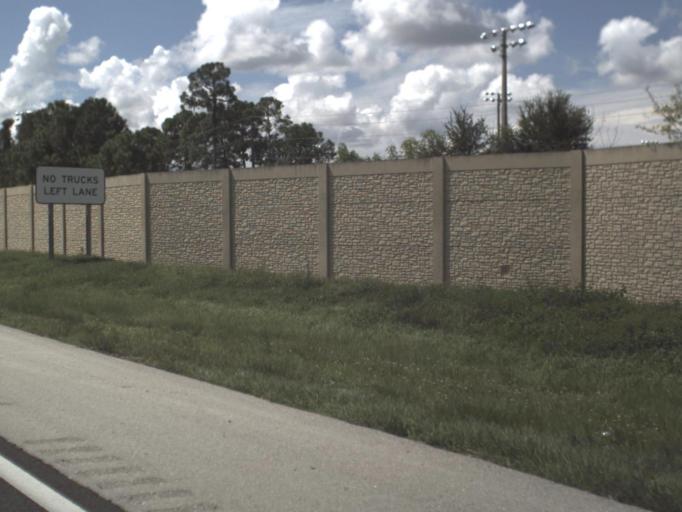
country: US
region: Florida
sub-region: Lee County
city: Three Oaks
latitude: 26.4756
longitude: -81.7920
